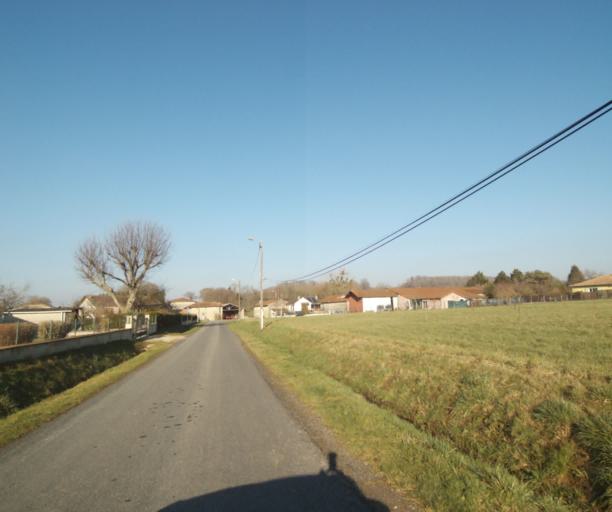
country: FR
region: Champagne-Ardenne
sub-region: Departement de la Haute-Marne
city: Bienville
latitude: 48.5399
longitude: 5.0187
